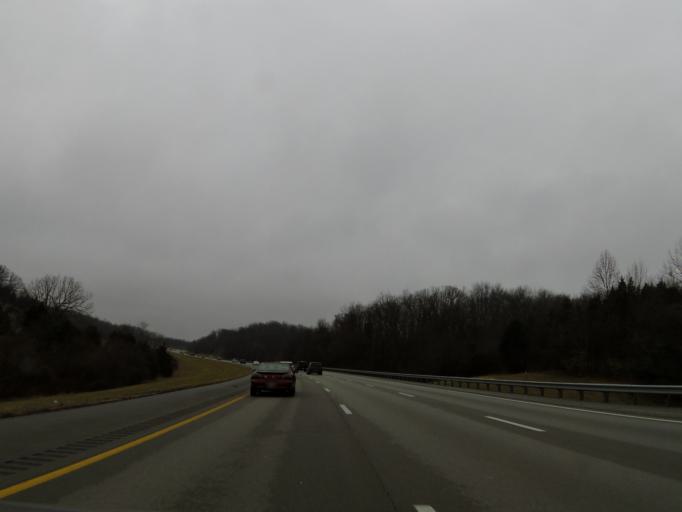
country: US
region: Kentucky
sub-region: Scott County
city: Georgetown
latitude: 38.3275
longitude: -84.5634
